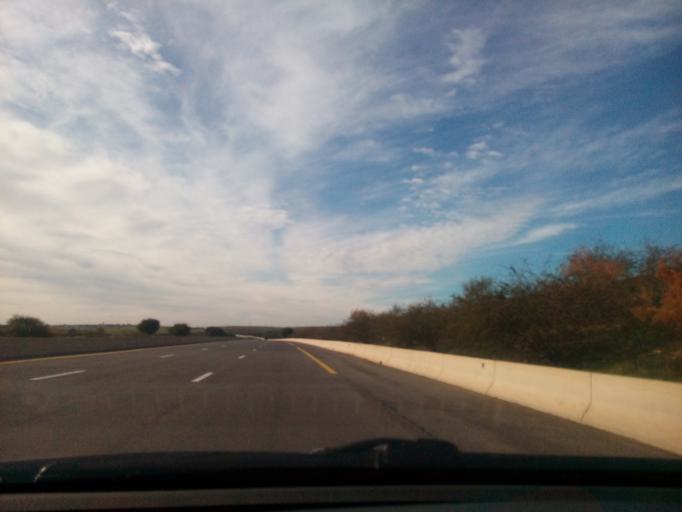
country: DZ
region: Sidi Bel Abbes
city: Sidi Bel Abbes
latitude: 35.1661
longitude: -0.7680
